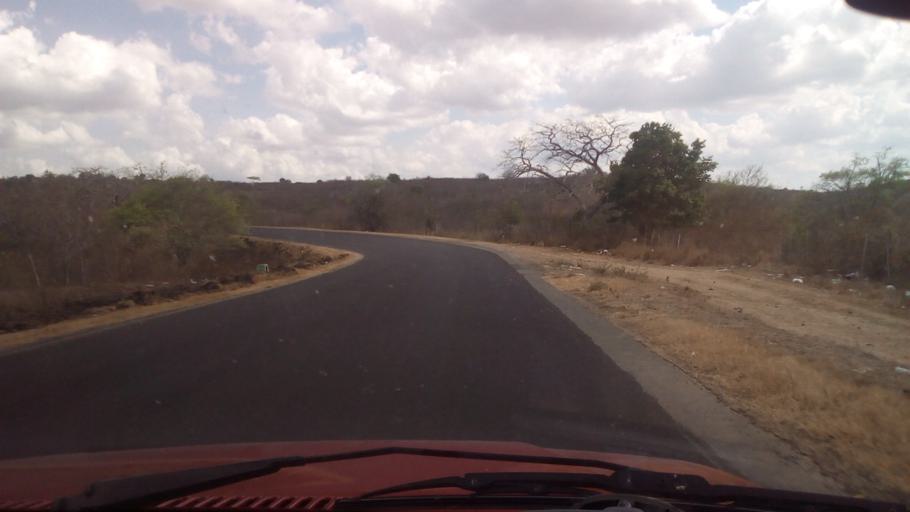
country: BR
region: Paraiba
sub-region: Bananeiras
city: Bananeiras
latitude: -6.7440
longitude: -35.7181
